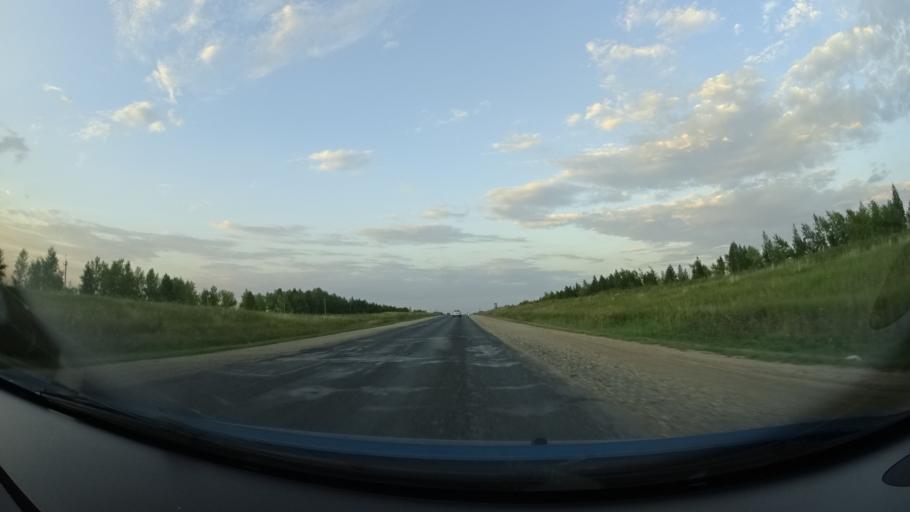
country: RU
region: Orenburg
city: Severnoye
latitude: 54.2159
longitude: 52.7203
